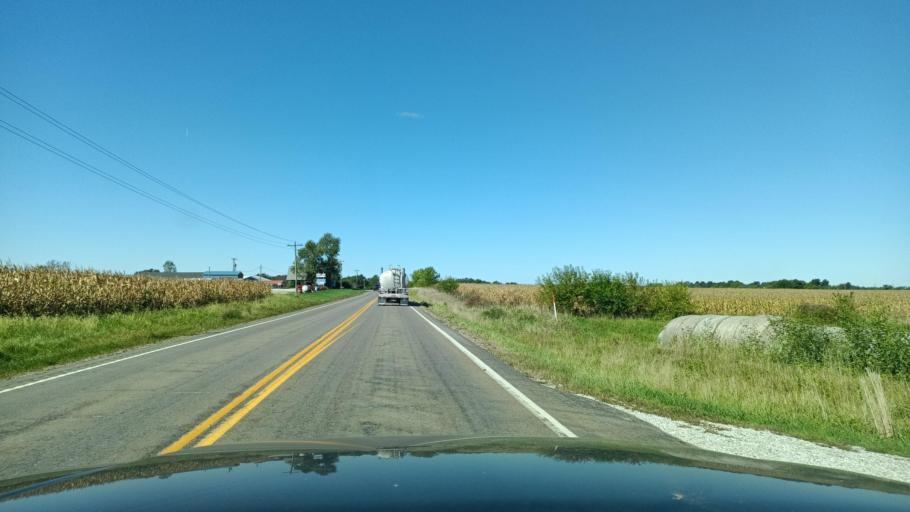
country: US
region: Missouri
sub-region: Scotland County
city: Memphis
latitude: 40.4551
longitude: -92.0499
